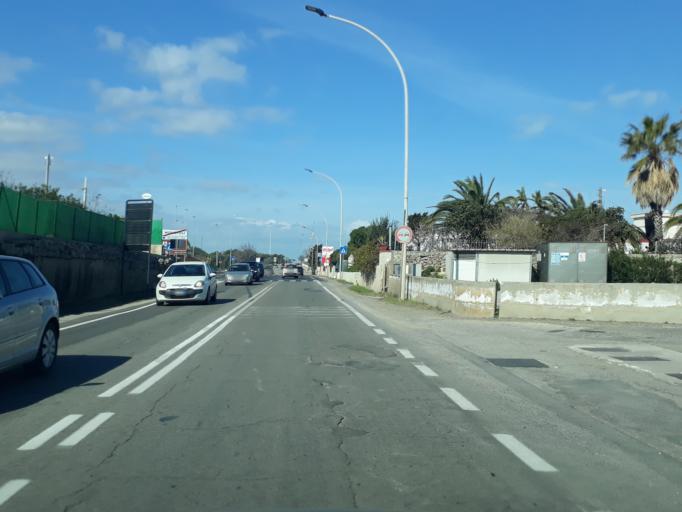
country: IT
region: Apulia
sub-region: Provincia di Bari
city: Monopoli
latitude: 40.9702
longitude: 17.2655
